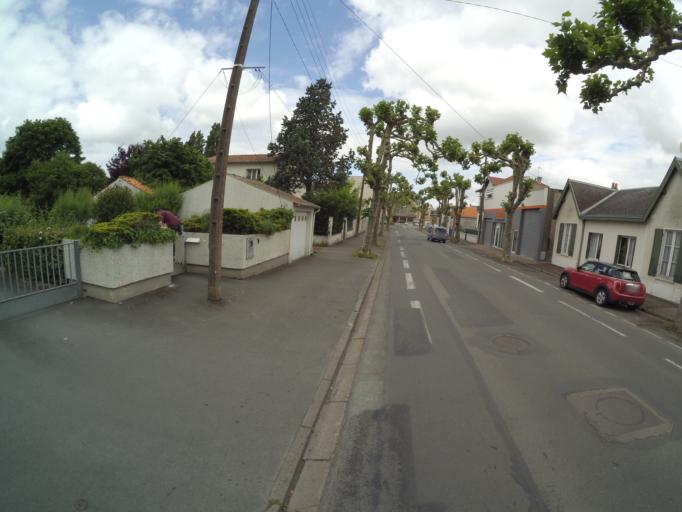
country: FR
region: Poitou-Charentes
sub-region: Departement de la Charente-Maritime
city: Rochefort
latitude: 45.9458
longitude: -0.9626
